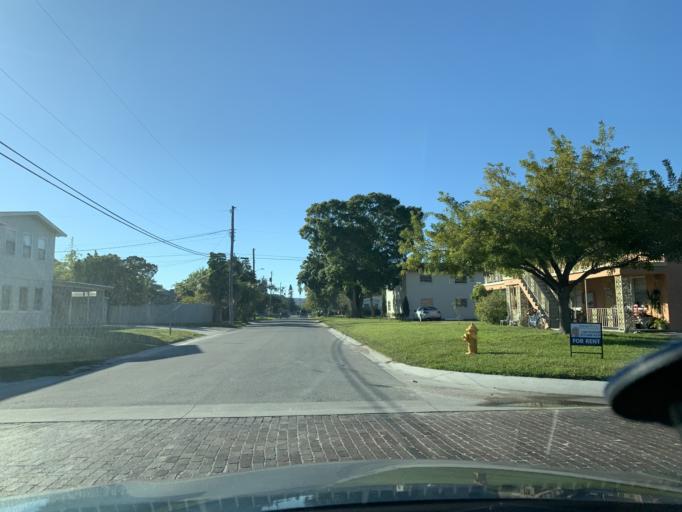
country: US
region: Florida
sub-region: Pinellas County
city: Gulfport
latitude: 27.7389
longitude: -82.7087
